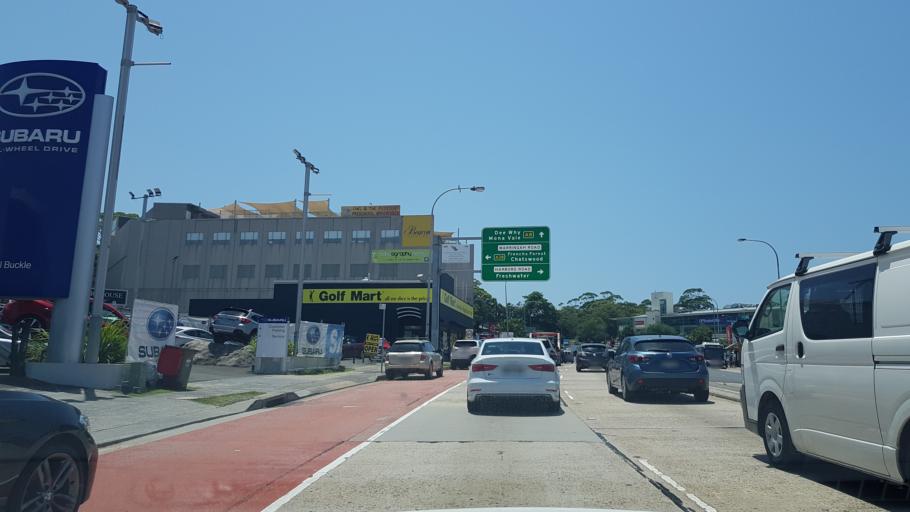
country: AU
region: New South Wales
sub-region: Warringah
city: Brookvale
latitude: -33.7596
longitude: 151.2788
